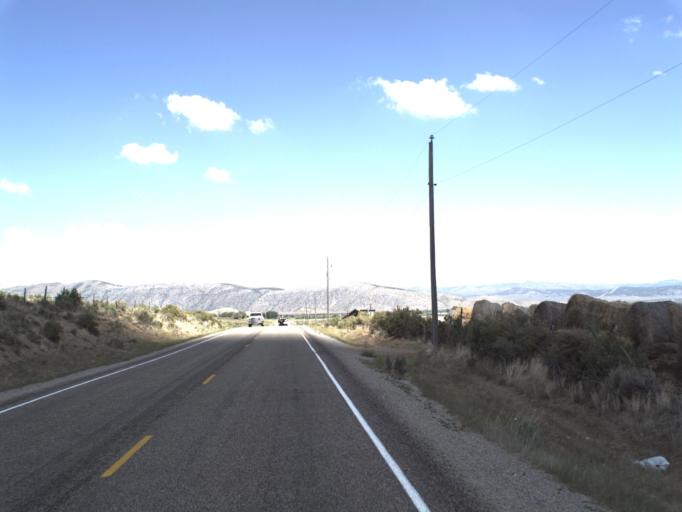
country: US
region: Utah
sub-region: Rich County
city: Randolph
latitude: 41.5202
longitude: -111.1945
